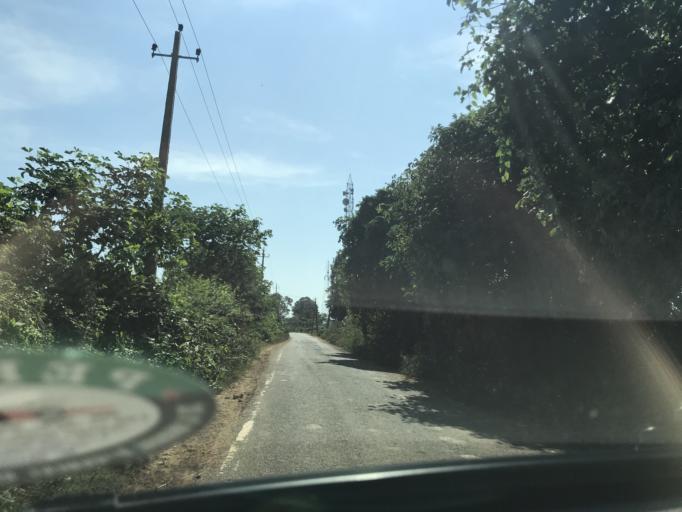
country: IN
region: Karnataka
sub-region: Mysore
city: Sargur
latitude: 11.9451
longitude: 76.2657
